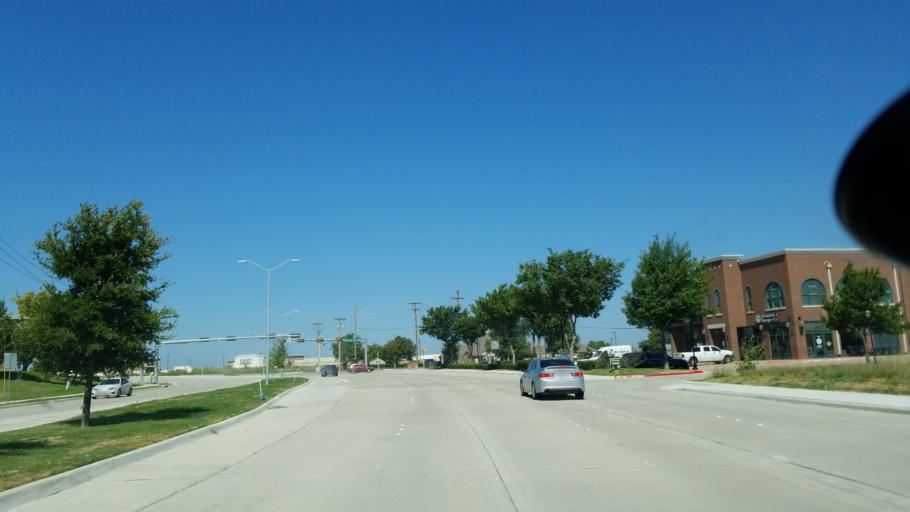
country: US
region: Texas
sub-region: Tarrant County
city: Mansfield
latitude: 32.5715
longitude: -97.1077
